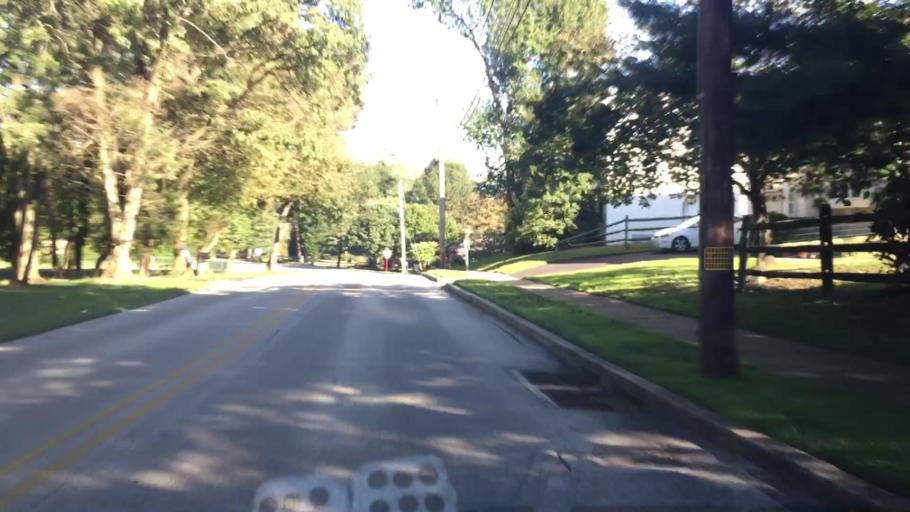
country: US
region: Pennsylvania
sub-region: Delaware County
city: Village Green-Green Ridge
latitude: 39.8694
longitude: -75.4467
